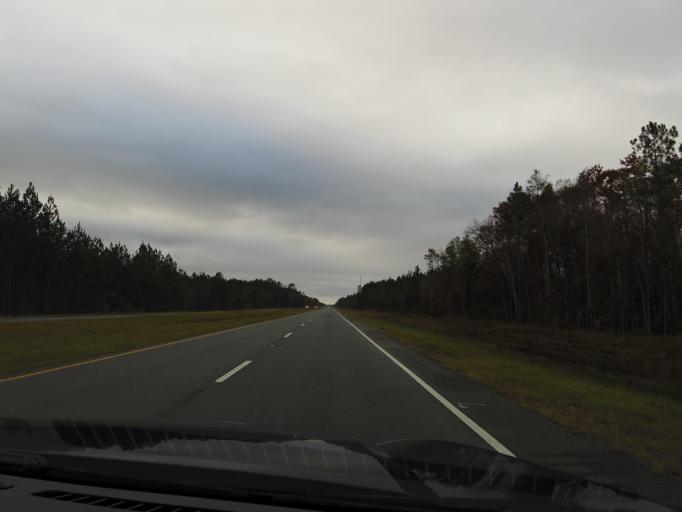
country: US
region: Georgia
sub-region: Charlton County
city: Folkston
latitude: 30.8964
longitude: -82.0562
